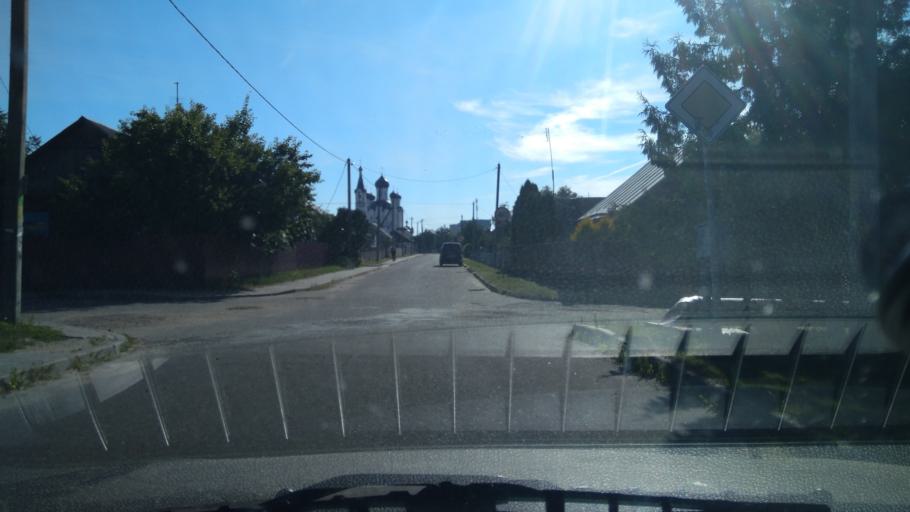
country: BY
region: Brest
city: Ivatsevichy
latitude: 52.7129
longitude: 25.3369
